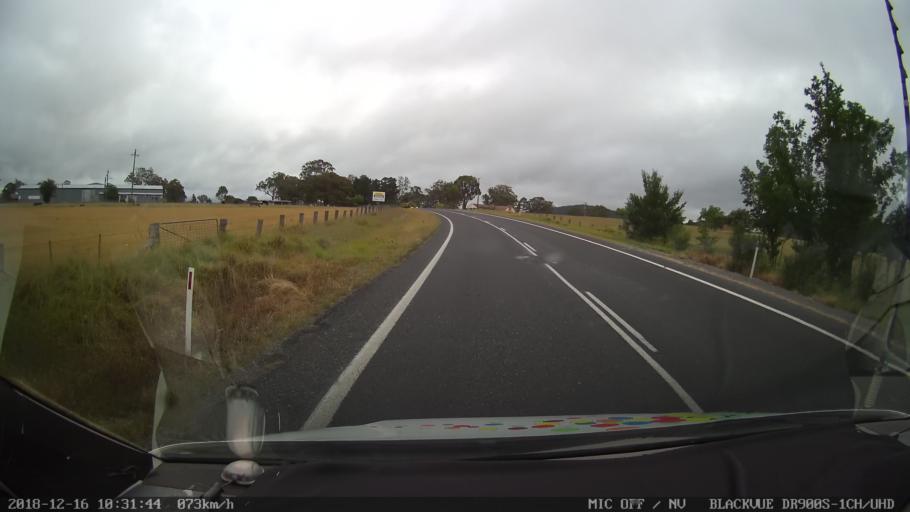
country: AU
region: New South Wales
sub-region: Tenterfield Municipality
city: Carrolls Creek
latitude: -29.0791
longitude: 152.0080
